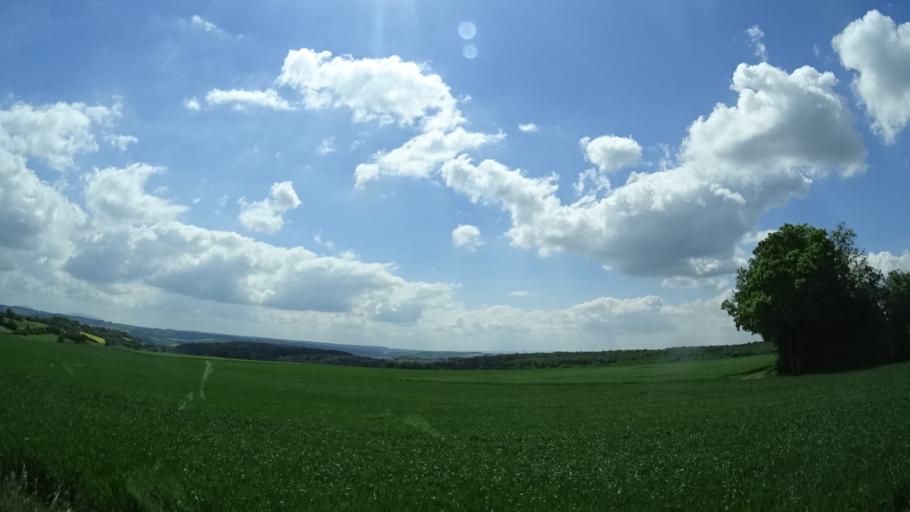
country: DE
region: Bavaria
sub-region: Regierungsbezirk Unterfranken
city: Stockheim
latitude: 50.4262
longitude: 10.2533
